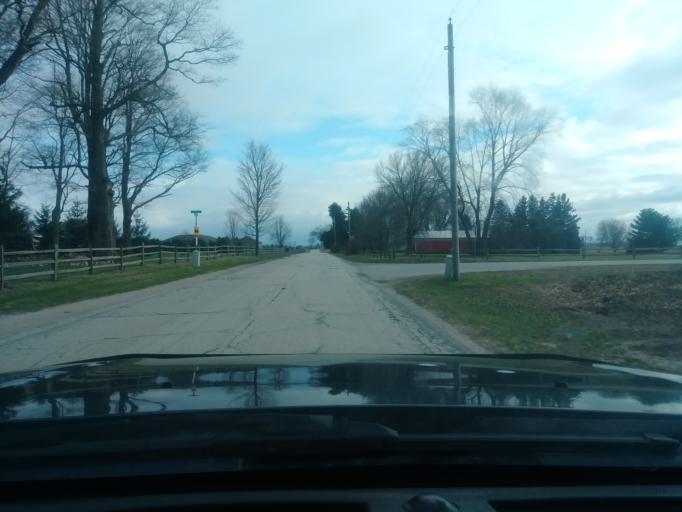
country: US
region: Indiana
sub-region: LaPorte County
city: LaPorte
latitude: 41.5696
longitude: -86.7983
